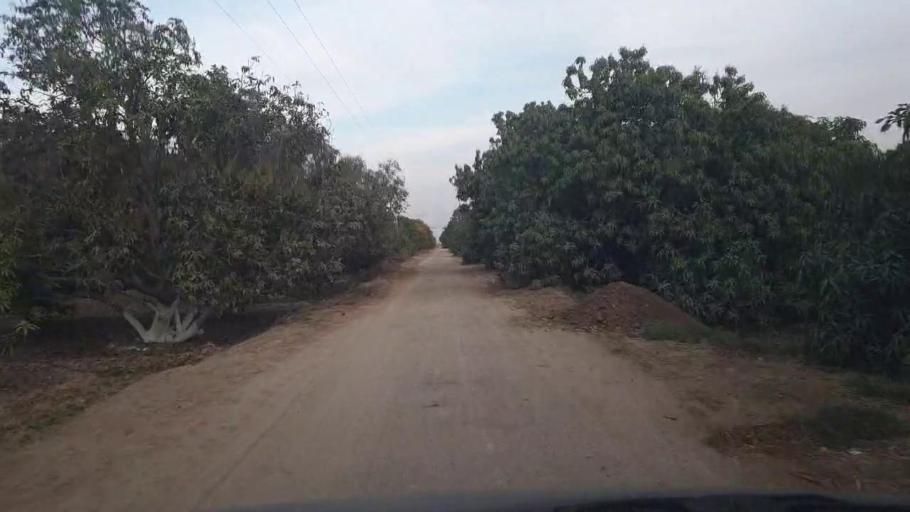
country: PK
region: Sindh
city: Kunri
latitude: 25.2385
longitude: 69.5615
